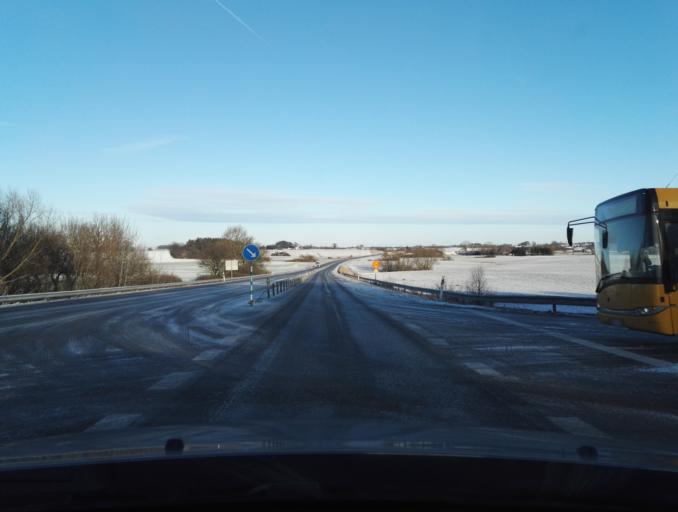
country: SE
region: Skane
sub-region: Svedala Kommun
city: Svedala
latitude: 55.4777
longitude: 13.2150
